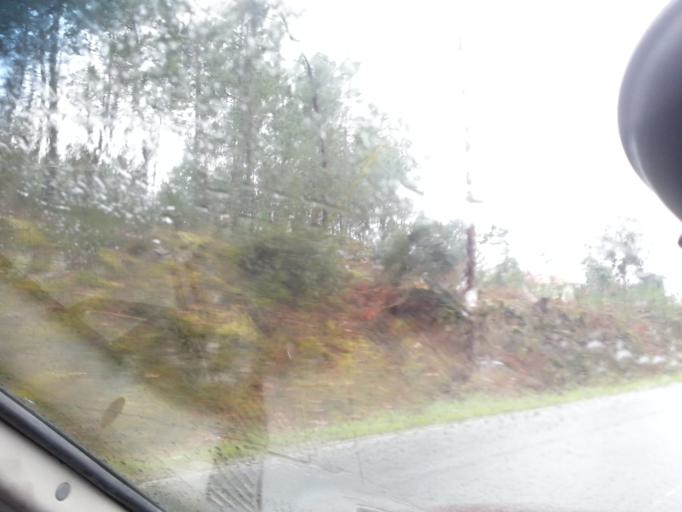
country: PT
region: Viseu
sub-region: Mangualde
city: Mangualde
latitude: 40.6114
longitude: -7.6739
